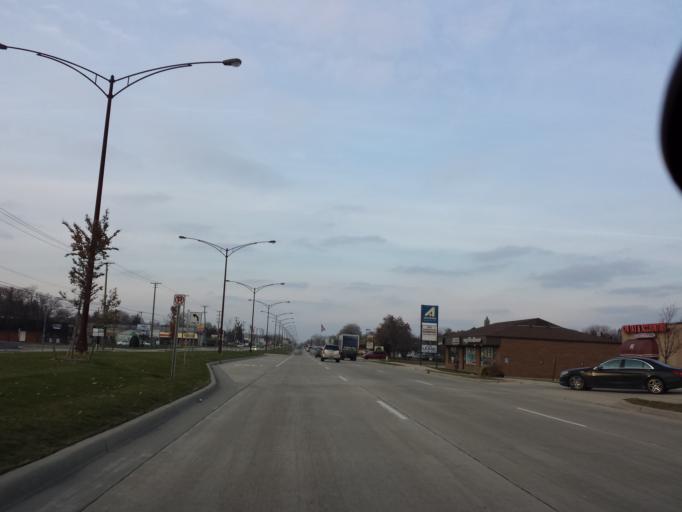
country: US
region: Michigan
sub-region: Oakland County
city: Clawson
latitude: 42.5692
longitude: -83.1279
